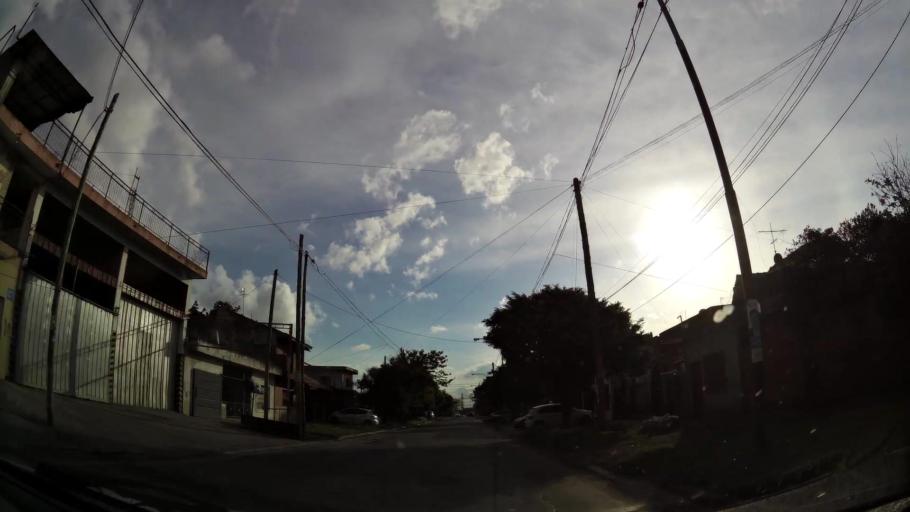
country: AR
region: Buenos Aires
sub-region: Partido de Quilmes
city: Quilmes
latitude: -34.7503
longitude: -58.2579
